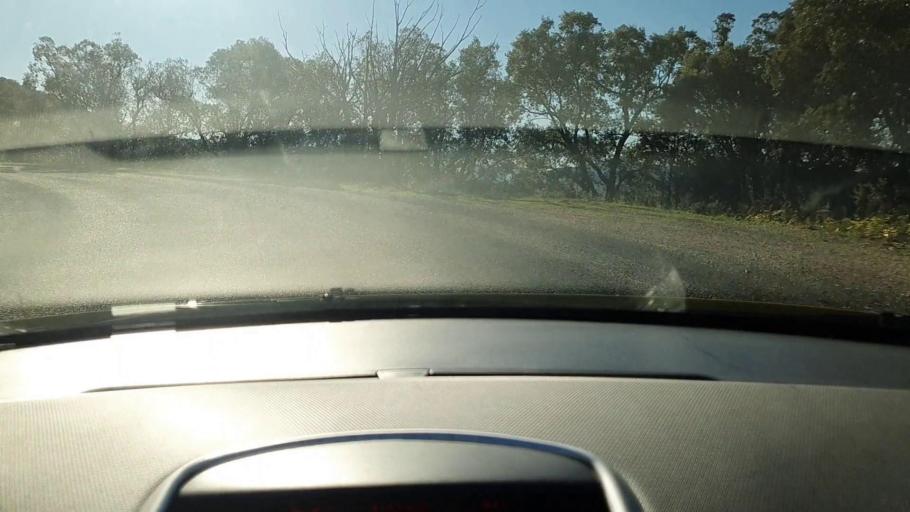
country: FR
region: Languedoc-Roussillon
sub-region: Departement du Gard
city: Sumene
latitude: 44.0299
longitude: 3.6911
